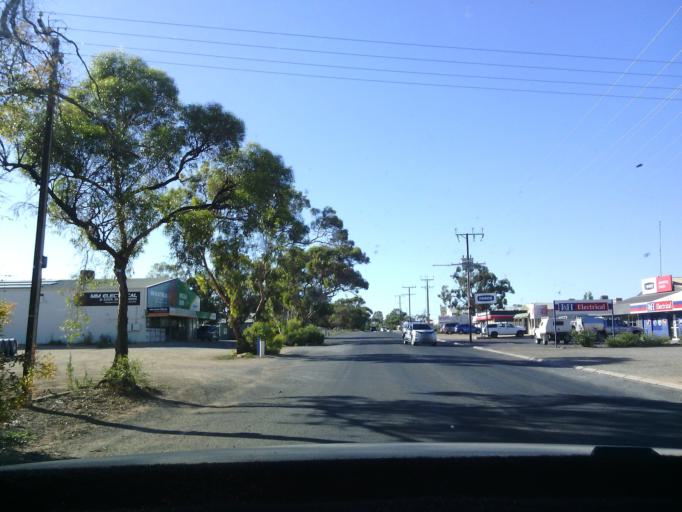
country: AU
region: South Australia
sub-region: Berri and Barmera
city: Berri
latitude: -34.2682
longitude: 140.6032
